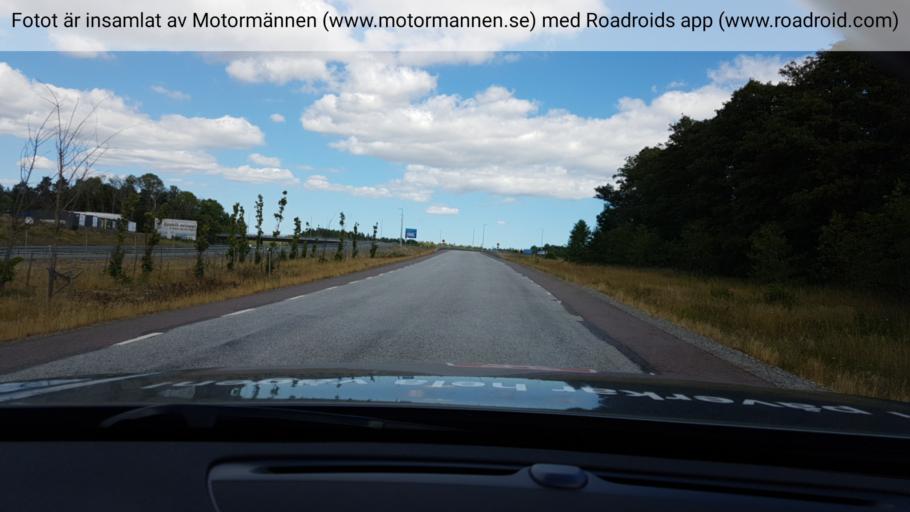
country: SE
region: Stockholm
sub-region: Haninge Kommun
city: Jordbro
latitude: 59.0654
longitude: 18.0597
